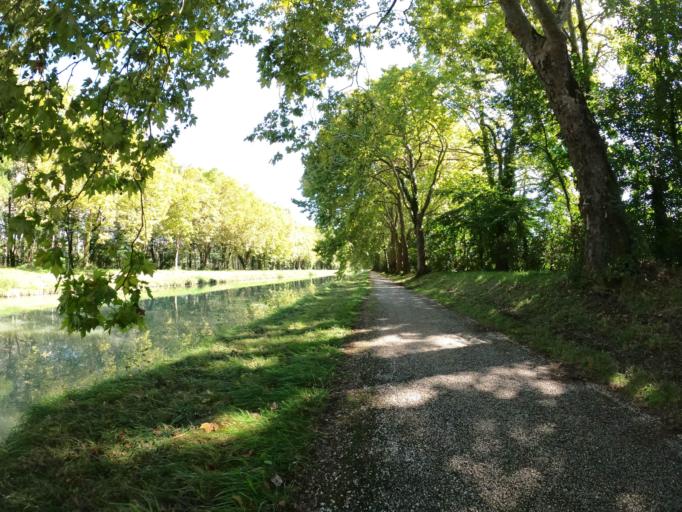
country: FR
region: Midi-Pyrenees
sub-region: Departement du Tarn-et-Garonne
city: Valence
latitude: 44.1114
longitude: 0.8727
